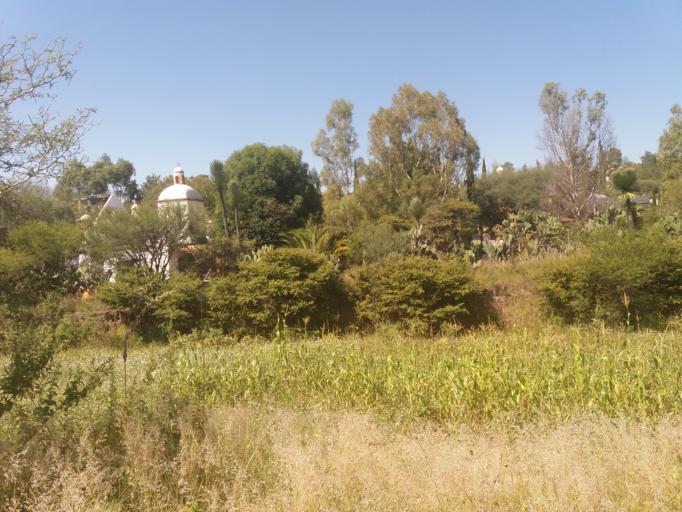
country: MX
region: Aguascalientes
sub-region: Aguascalientes
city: San Sebastian [Fraccionamiento]
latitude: 21.7819
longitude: -102.2313
